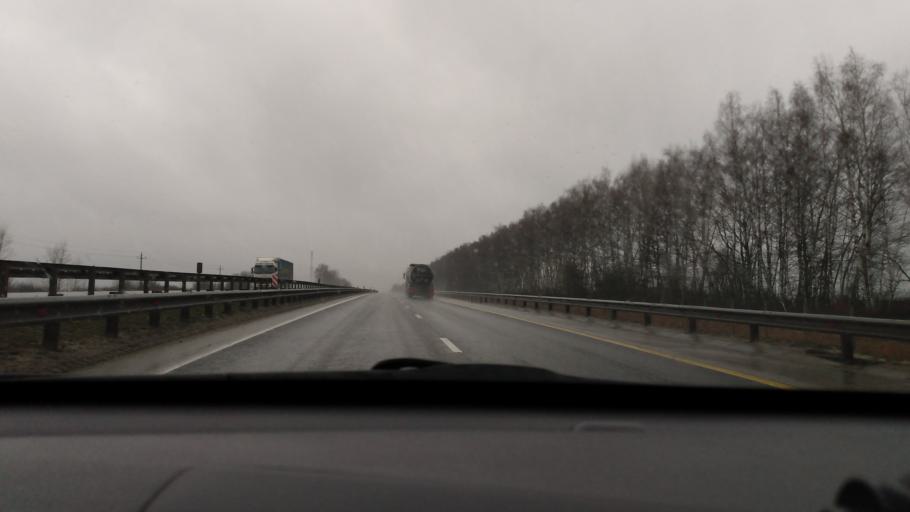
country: RU
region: Tula
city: Venev
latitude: 54.4029
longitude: 38.1646
